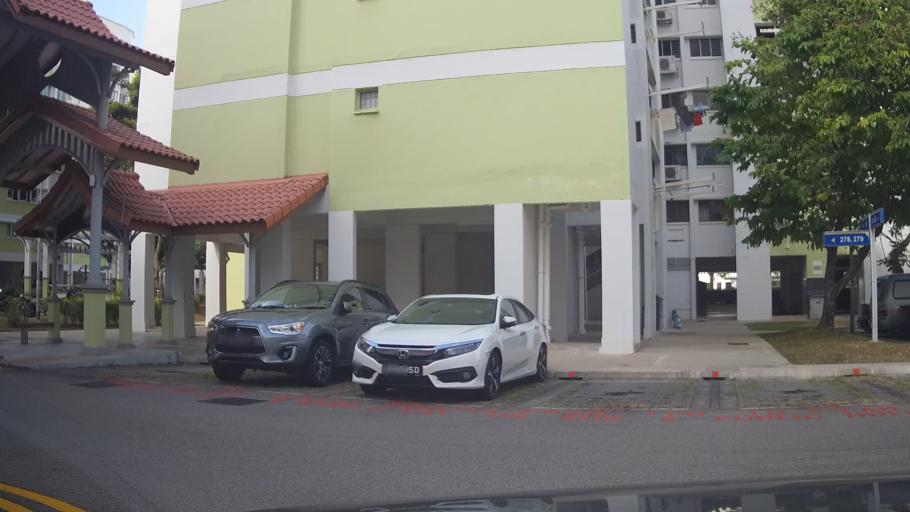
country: SG
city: Singapore
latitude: 1.3473
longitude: 103.9523
